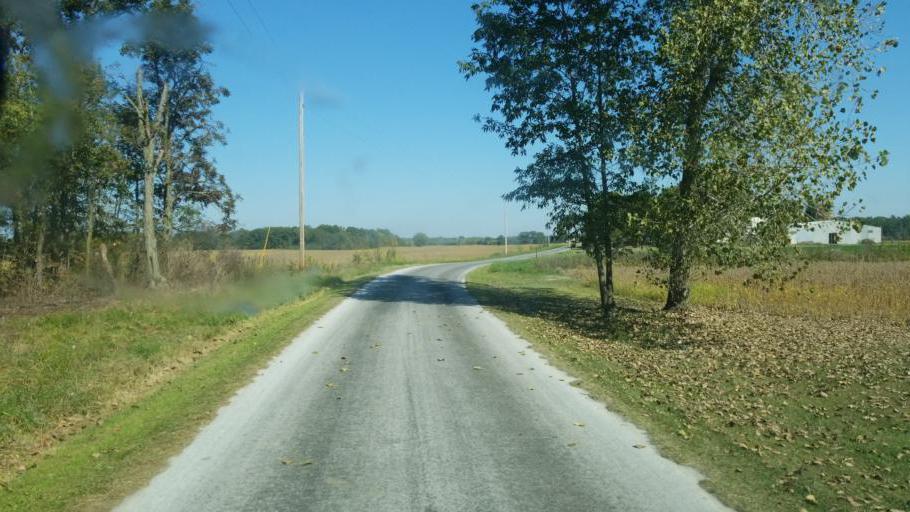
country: US
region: Ohio
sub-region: Hardin County
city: Kenton
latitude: 40.5740
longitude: -83.4885
